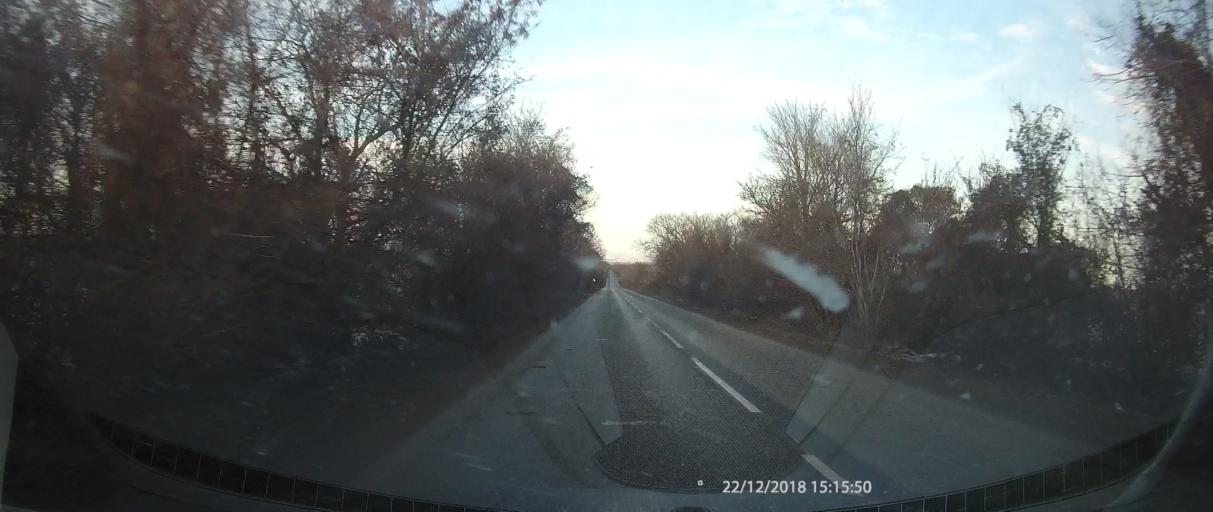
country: BG
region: Ruse
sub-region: Obshtina Dve Mogili
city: Dve Mogili
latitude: 43.5970
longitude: 25.8397
